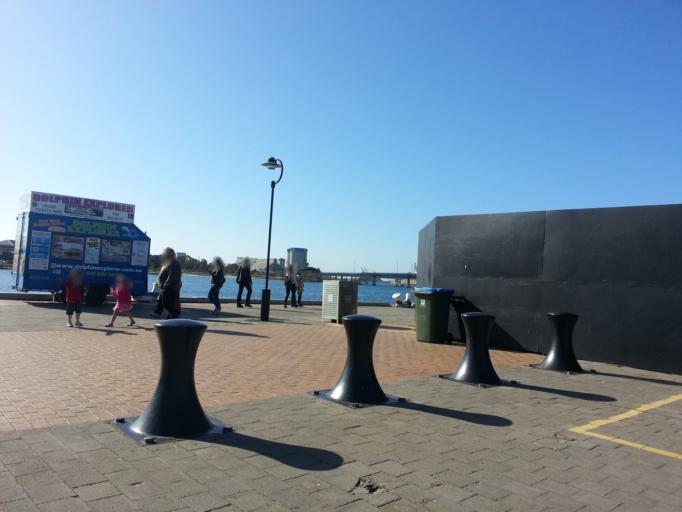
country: AU
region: South Australia
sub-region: Port Adelaide Enfield
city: Birkenhead
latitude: -34.8424
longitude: 138.5044
